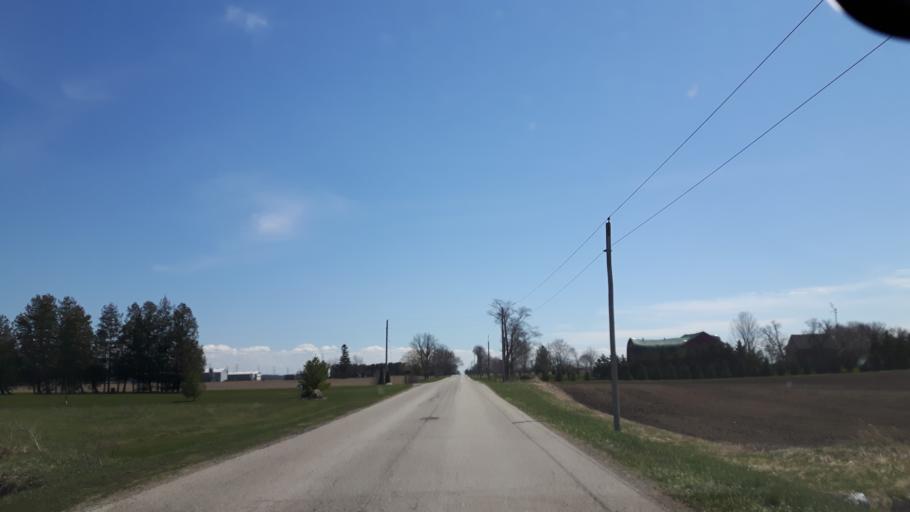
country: CA
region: Ontario
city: Goderich
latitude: 43.6354
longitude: -81.6440
